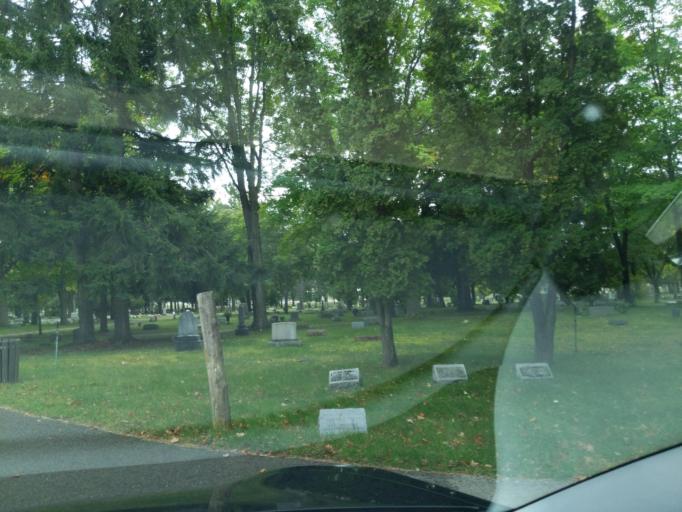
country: US
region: Michigan
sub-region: Grand Traverse County
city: Traverse City
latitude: 44.7550
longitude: -85.5877
